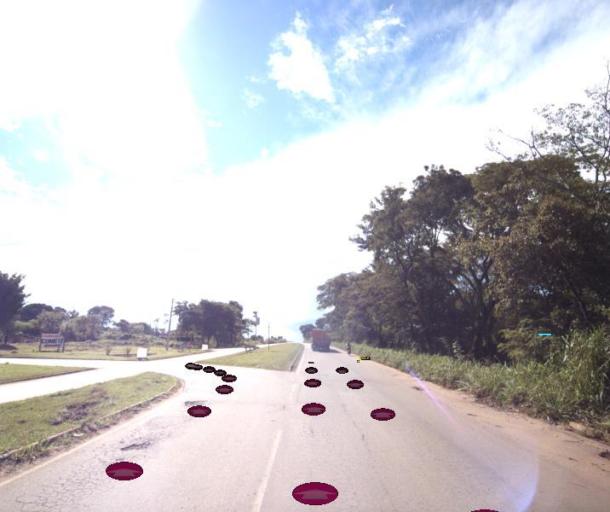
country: BR
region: Goias
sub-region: Jaragua
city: Jaragua
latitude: -15.7588
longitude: -49.3132
